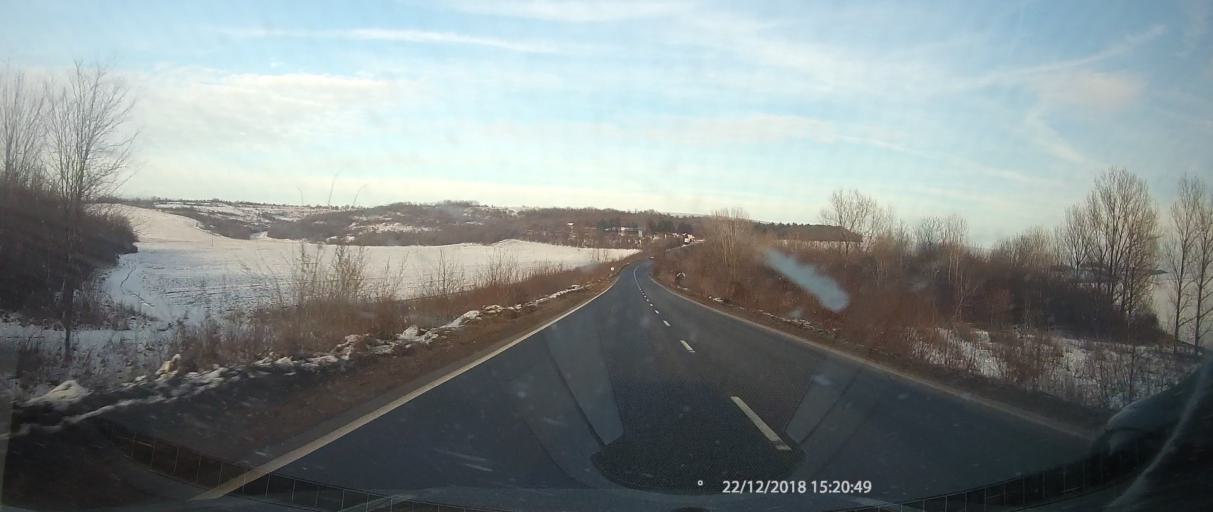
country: BG
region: Ruse
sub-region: Obshtina Dve Mogili
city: Dve Mogili
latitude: 43.6753
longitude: 25.8928
